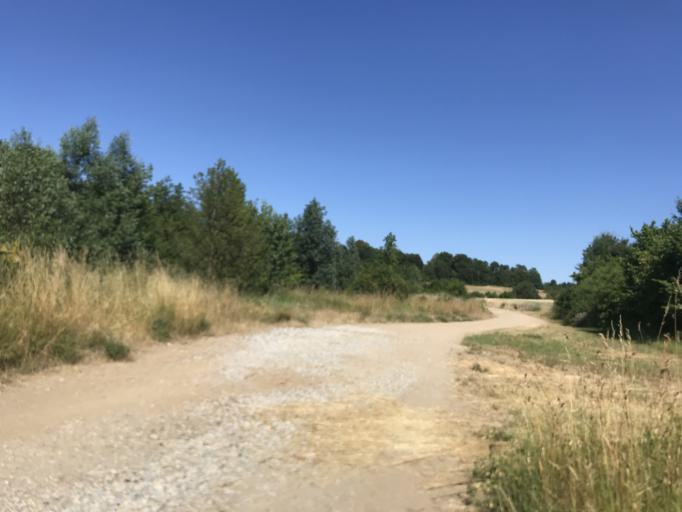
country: DE
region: Rheinland-Pfalz
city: Mainz
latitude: 49.9725
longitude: 8.2600
